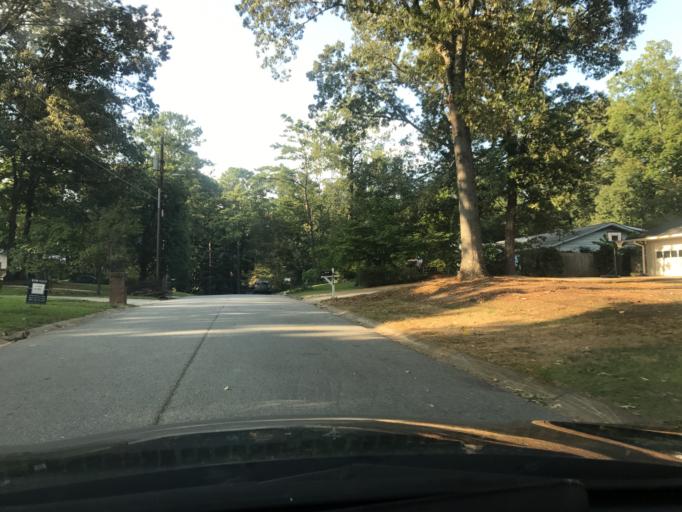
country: US
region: Georgia
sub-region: DeKalb County
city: North Druid Hills
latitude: 33.8242
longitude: -84.2795
